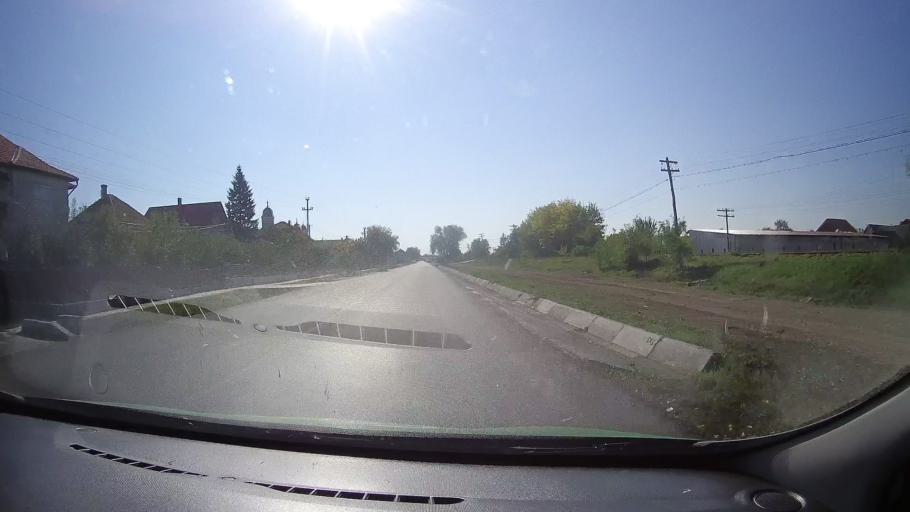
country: RO
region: Satu Mare
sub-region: Comuna Berveni
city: Lucaceni
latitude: 47.7435
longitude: 22.4744
